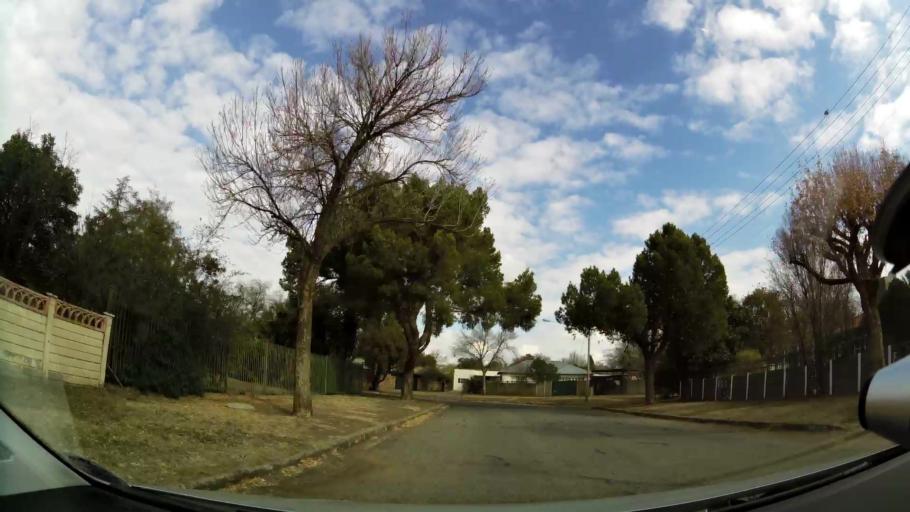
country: ZA
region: Orange Free State
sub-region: Mangaung Metropolitan Municipality
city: Bloemfontein
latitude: -29.0894
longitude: 26.2460
